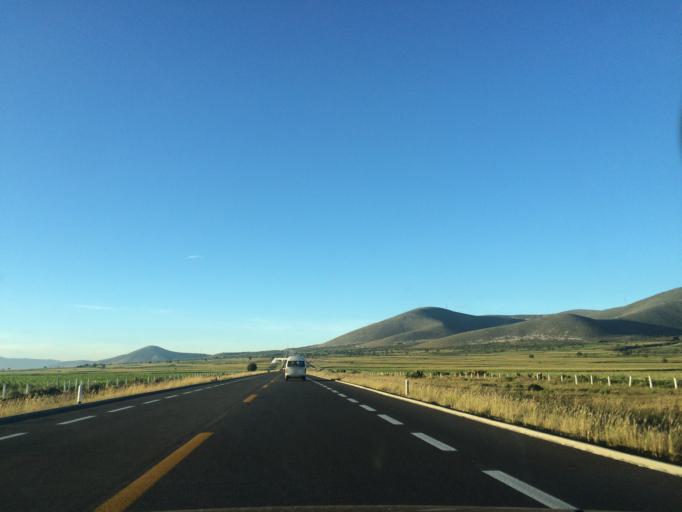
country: MX
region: Puebla
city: Morelos Canada
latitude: 18.7507
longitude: -97.4800
